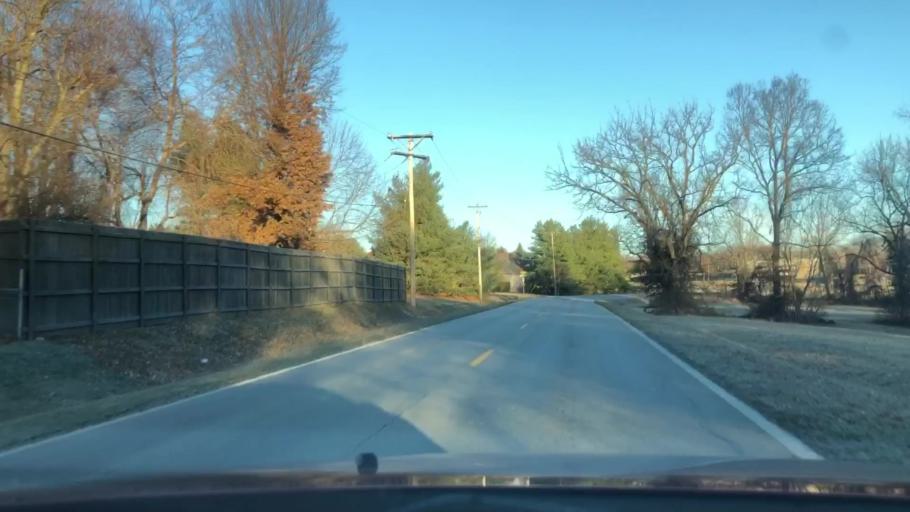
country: US
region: Missouri
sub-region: Greene County
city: Springfield
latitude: 37.1655
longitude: -93.2457
